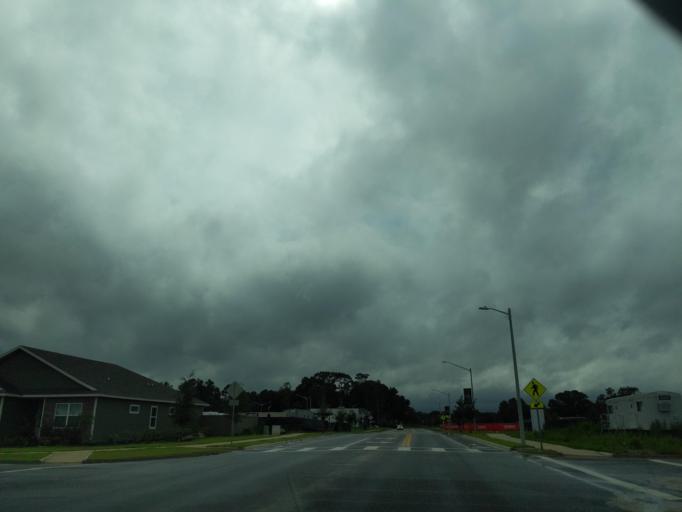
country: US
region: Florida
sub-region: Alachua County
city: Gainesville
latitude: 29.6381
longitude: -82.4198
